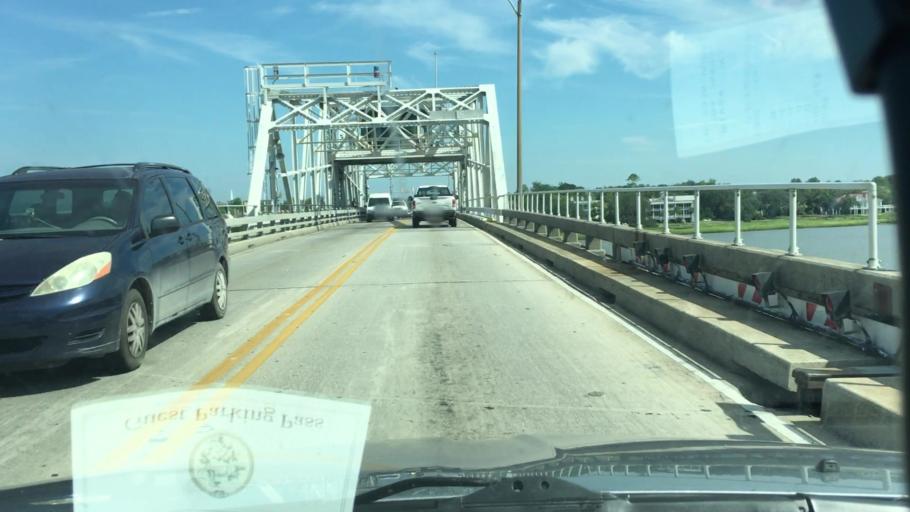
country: US
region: South Carolina
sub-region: Beaufort County
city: Beaufort
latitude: 32.4270
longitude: -80.6690
